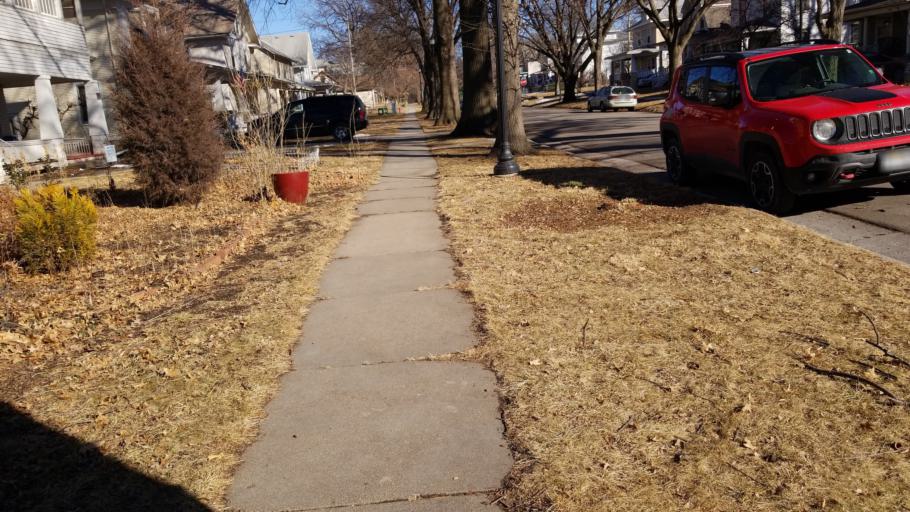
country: US
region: Nebraska
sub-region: Lancaster County
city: Lincoln
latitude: 40.8172
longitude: -96.6741
